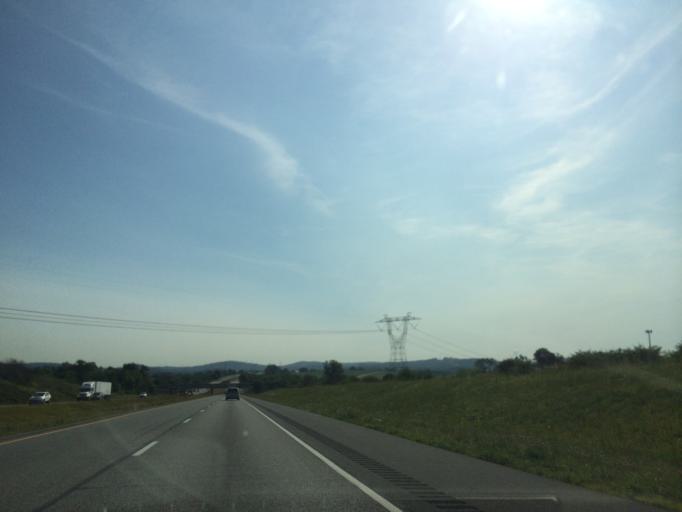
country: US
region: Pennsylvania
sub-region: Lancaster County
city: Reamstown
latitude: 40.2128
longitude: -76.0997
